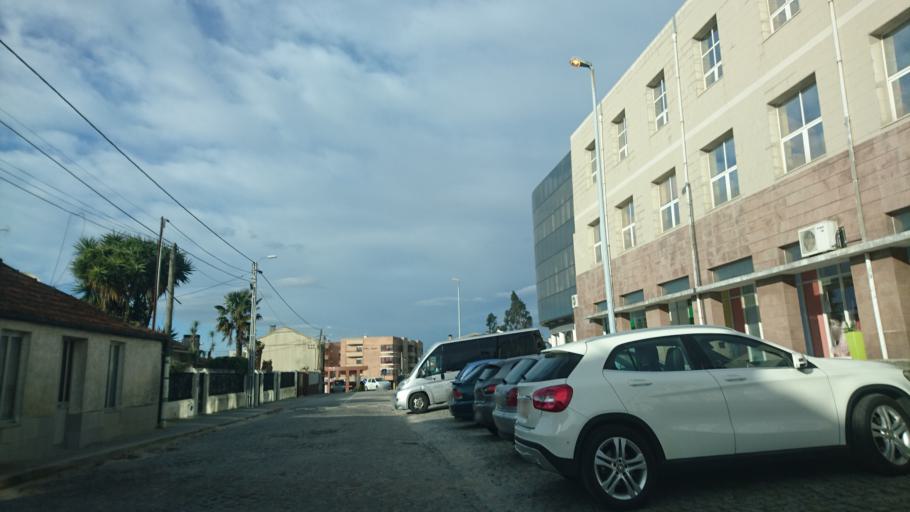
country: PT
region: Aveiro
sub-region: Santa Maria da Feira
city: Pacos de Brandao
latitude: 40.9728
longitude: -8.5789
